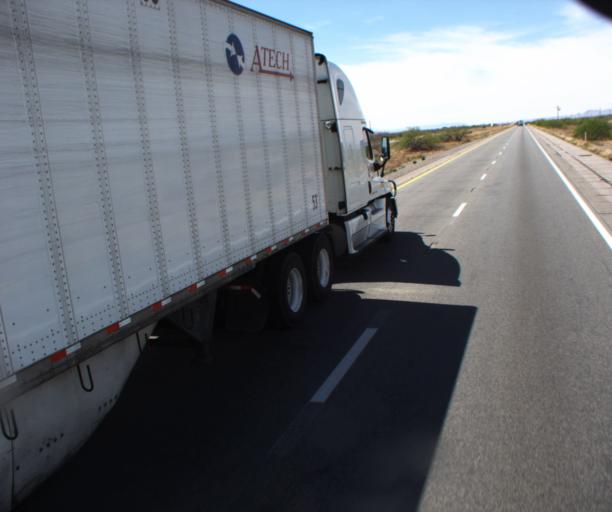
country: US
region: Arizona
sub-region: Cochise County
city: Willcox
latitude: 32.3010
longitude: -109.3694
